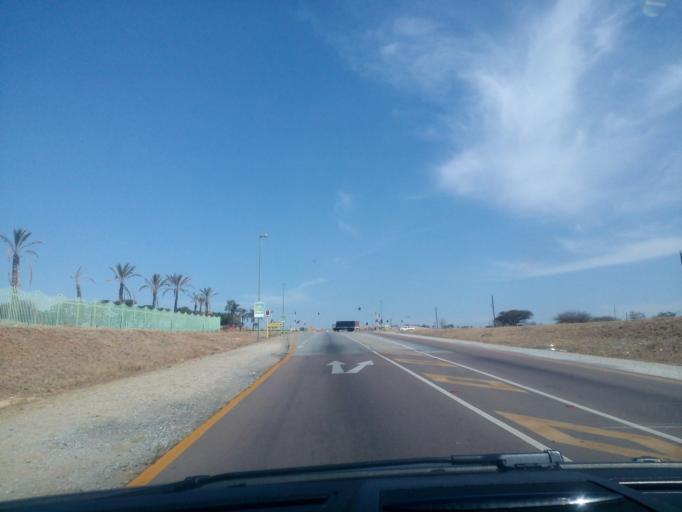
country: ZA
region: Limpopo
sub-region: Capricorn District Municipality
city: Polokwane
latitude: -23.9404
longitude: 29.4208
